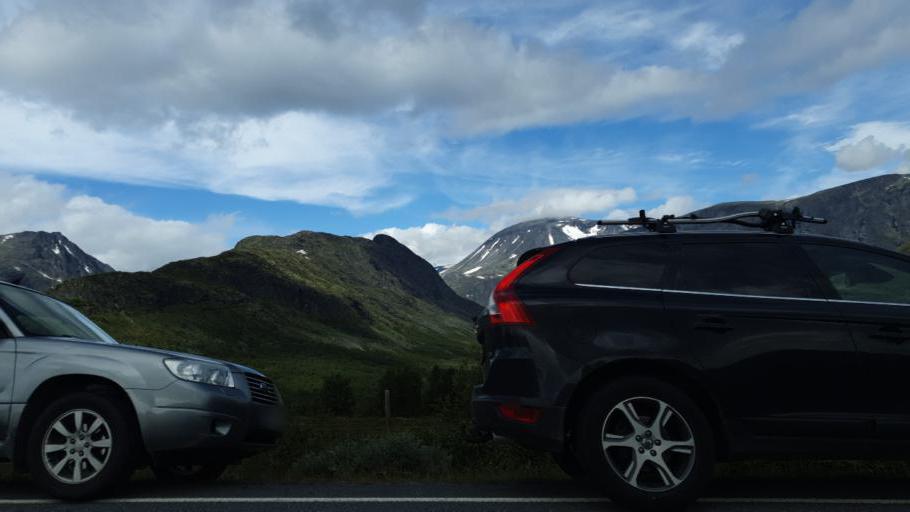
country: NO
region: Oppland
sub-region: Oystre Slidre
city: Heggenes
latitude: 61.4658
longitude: 8.8108
